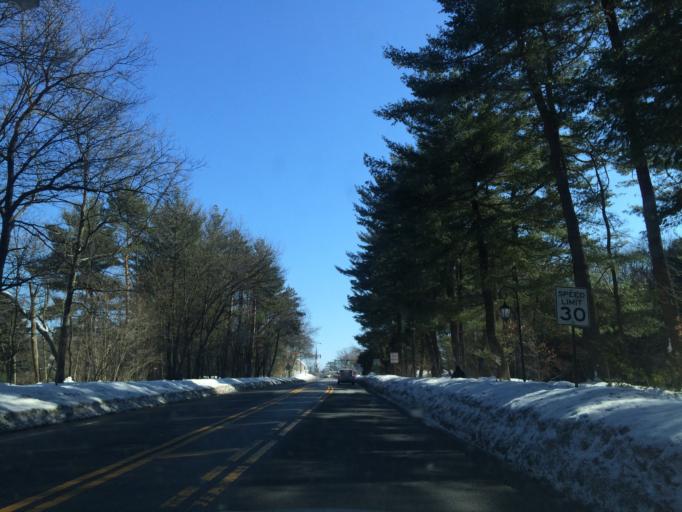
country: US
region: Massachusetts
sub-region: Norfolk County
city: Wellesley
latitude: 42.2961
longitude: -71.3016
